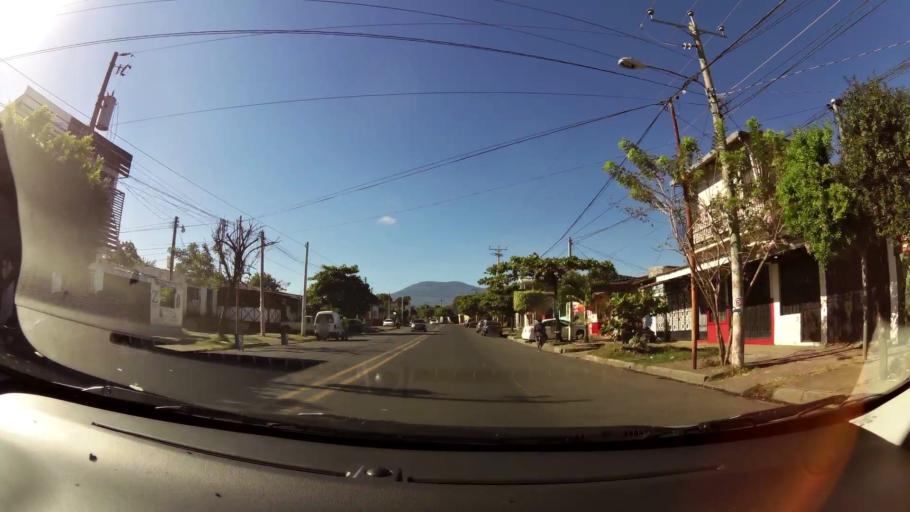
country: SV
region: Santa Ana
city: Santa Ana
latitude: 13.9680
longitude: -89.5737
